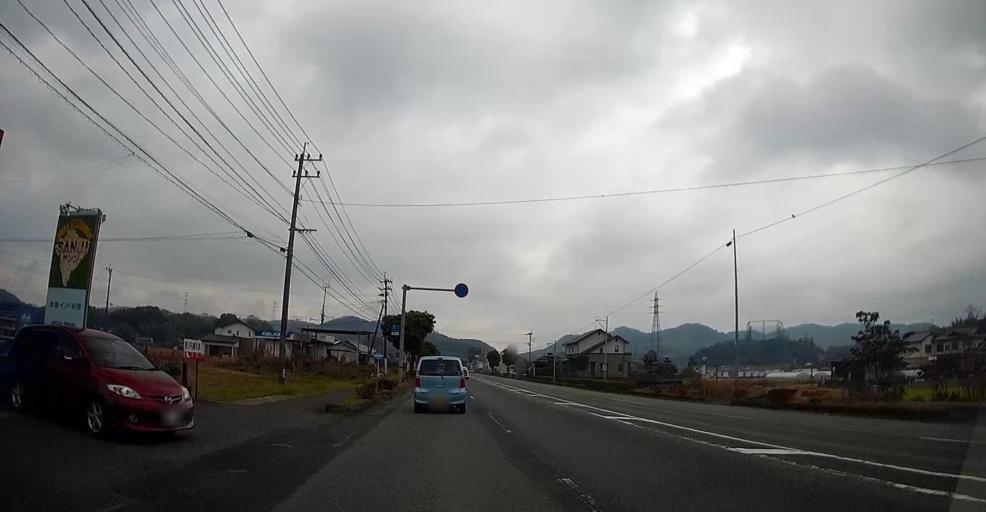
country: JP
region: Kumamoto
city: Matsubase
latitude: 32.6498
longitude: 130.7122
